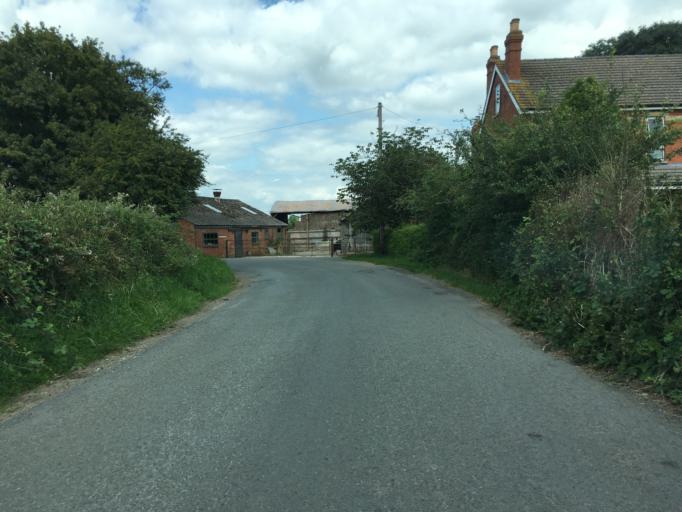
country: GB
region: England
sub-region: Gloucestershire
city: Gloucester
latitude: 51.9067
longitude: -2.2226
